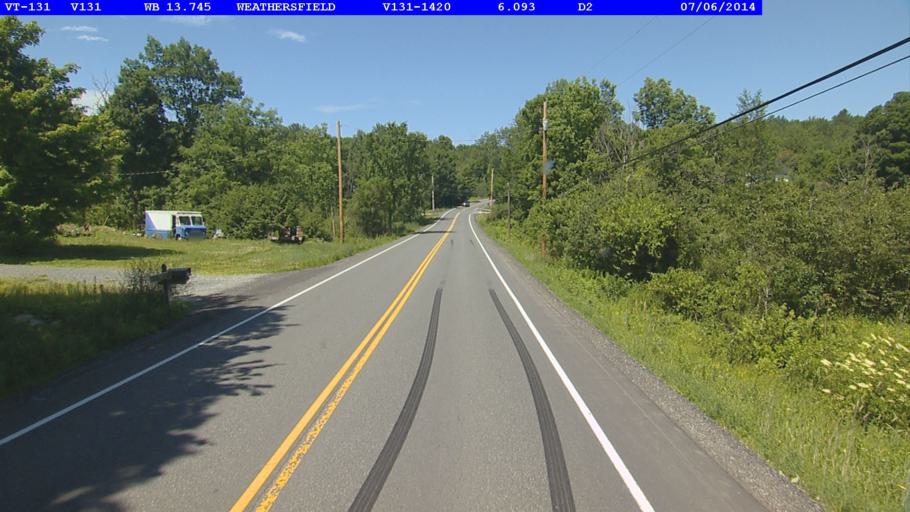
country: US
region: Vermont
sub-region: Windsor County
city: Windsor
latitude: 43.4121
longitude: -72.4515
